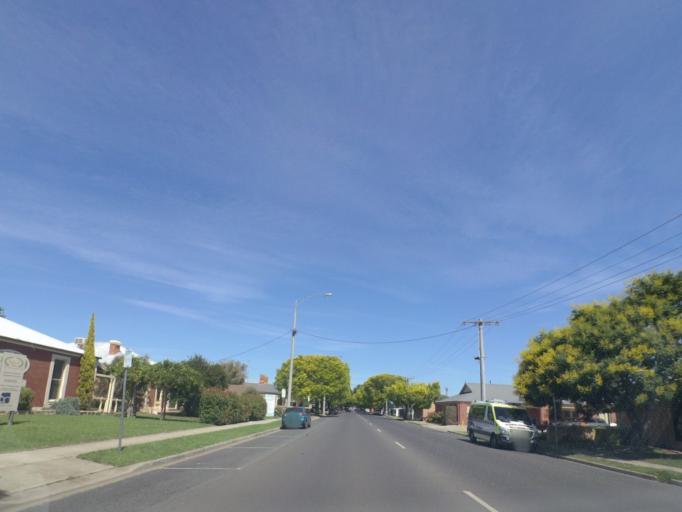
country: AU
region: Victoria
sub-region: Moorabool
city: Bacchus Marsh
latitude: -37.6767
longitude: 144.4434
